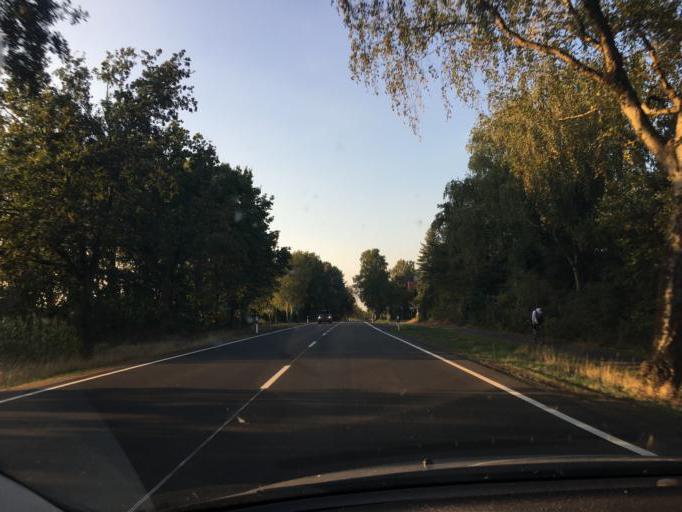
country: DE
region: Lower Saxony
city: Bergen
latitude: 52.7887
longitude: 9.9729
